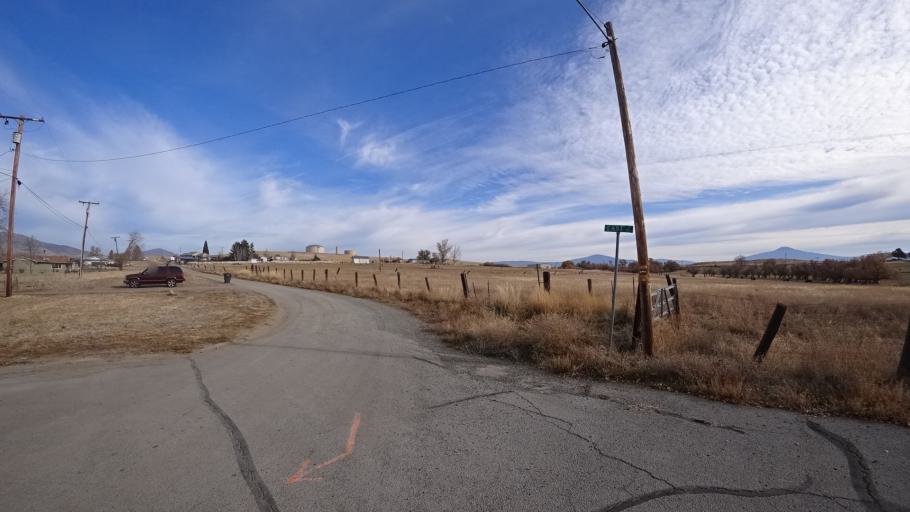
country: US
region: California
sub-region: Siskiyou County
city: Montague
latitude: 41.7272
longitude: -122.5156
